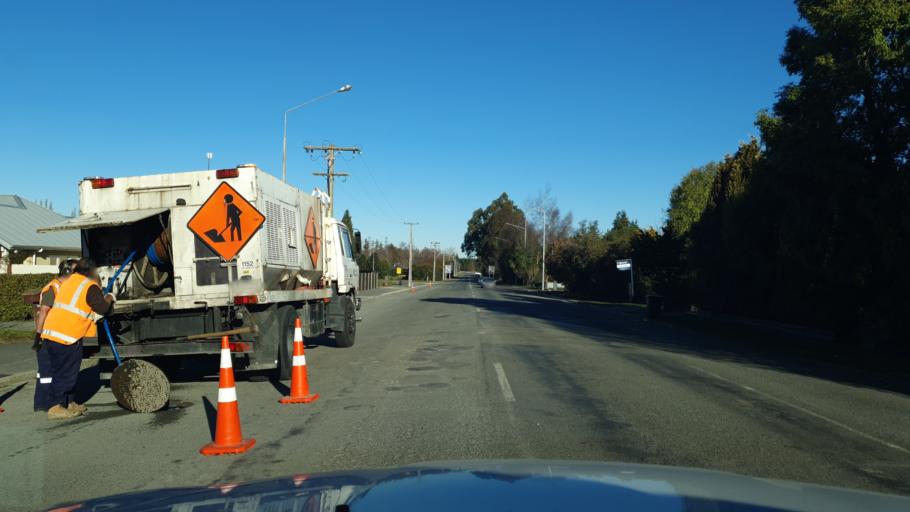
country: NZ
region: Canterbury
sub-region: Timaru District
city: Pleasant Point
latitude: -44.1097
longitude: 171.2451
